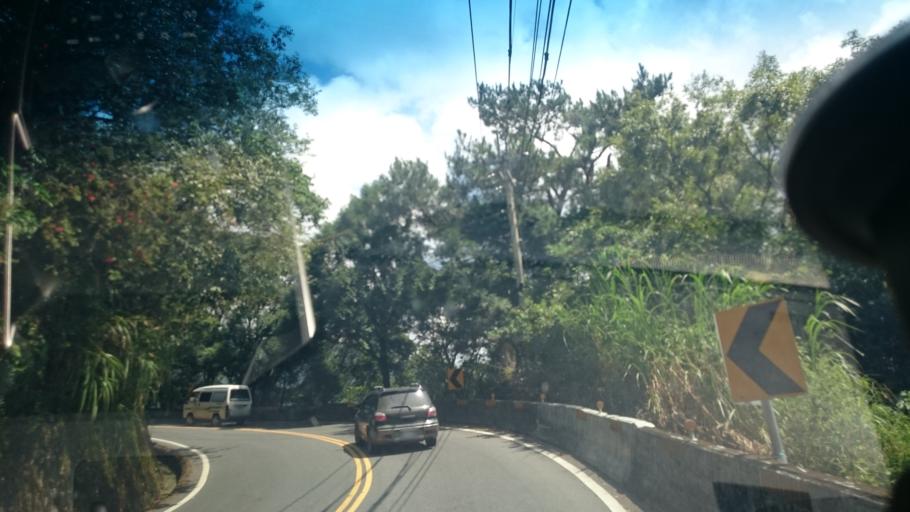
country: TW
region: Taiwan
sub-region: Nantou
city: Puli
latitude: 24.0264
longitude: 121.1432
